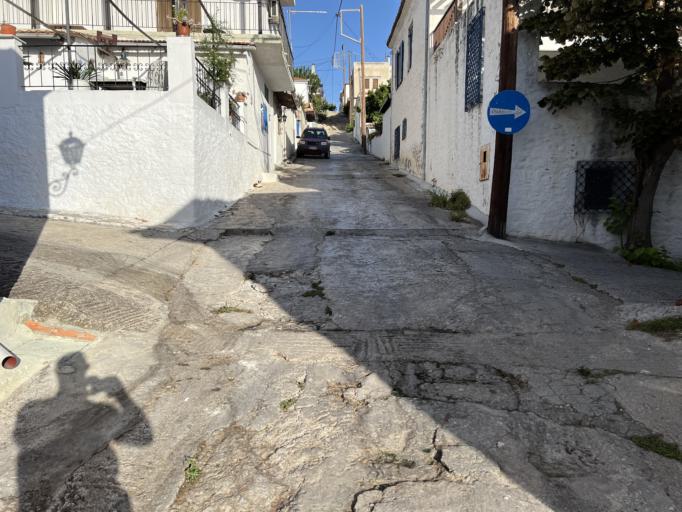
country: GR
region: Thessaly
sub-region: Nomos Magnisias
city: Sourpi
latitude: 39.1679
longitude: 22.8872
